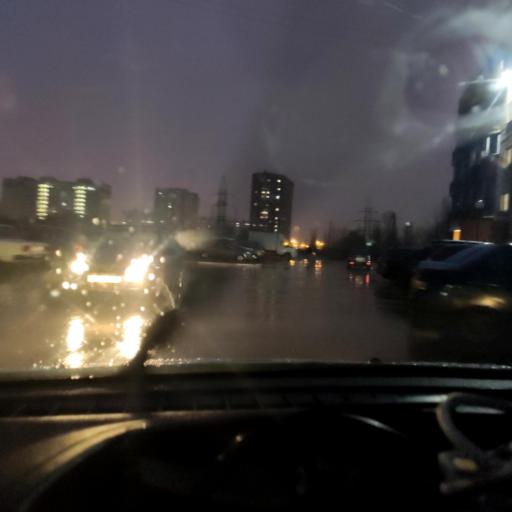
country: RU
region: Samara
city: Tol'yatti
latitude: 53.5452
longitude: 49.3946
